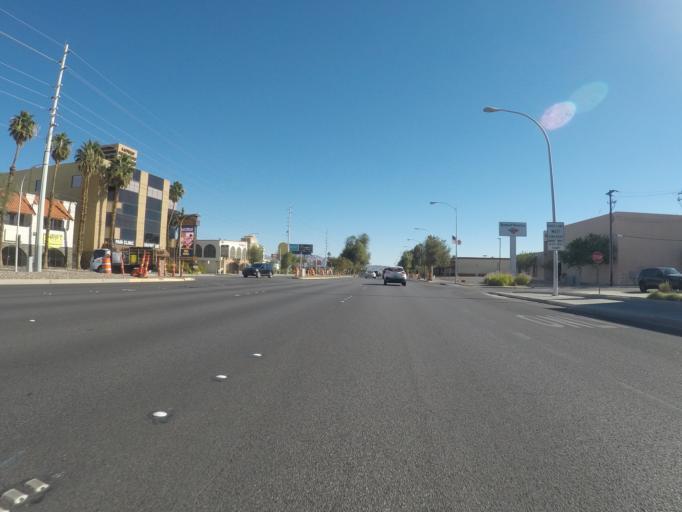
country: US
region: Nevada
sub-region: Clark County
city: Winchester
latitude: 36.1440
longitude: -115.1406
